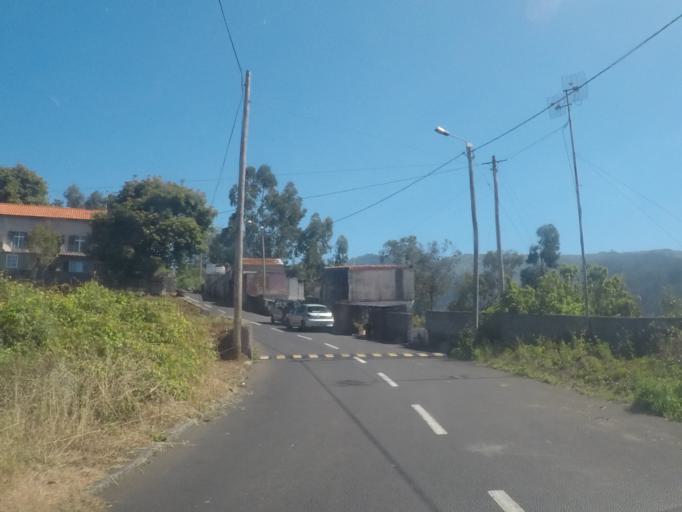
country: PT
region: Madeira
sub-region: Camara de Lobos
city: Curral das Freiras
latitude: 32.6805
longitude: -16.9672
